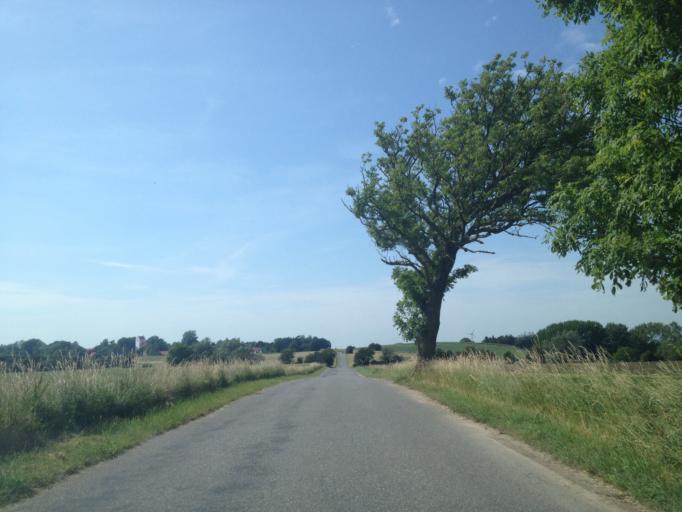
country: DK
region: Central Jutland
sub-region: Samso Kommune
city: Tranebjerg
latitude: 55.7960
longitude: 10.5694
